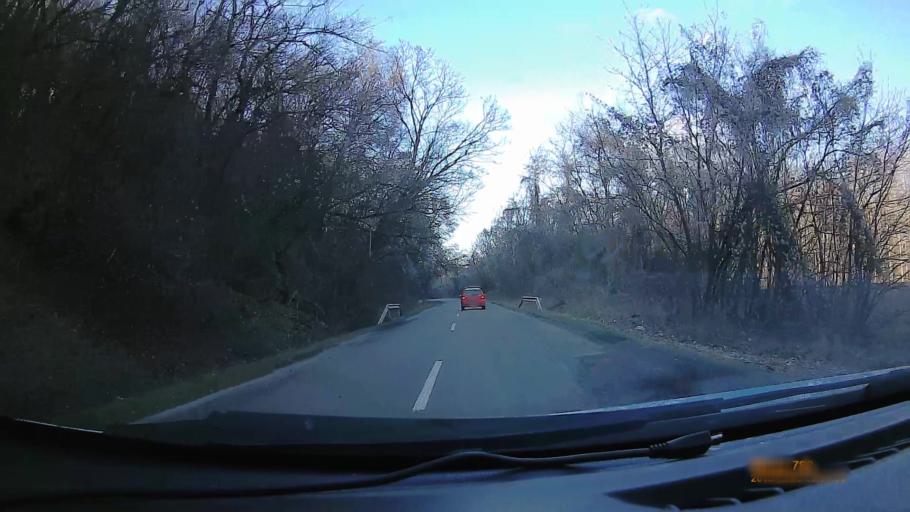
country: HU
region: Heves
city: Sirok
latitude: 47.8828
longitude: 20.1936
